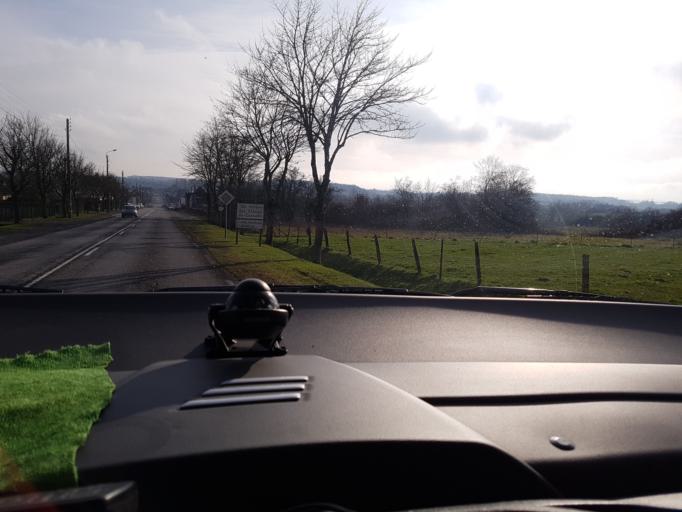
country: FR
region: Picardie
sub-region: Departement de l'Aisne
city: Hirson
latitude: 49.9357
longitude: 4.0721
